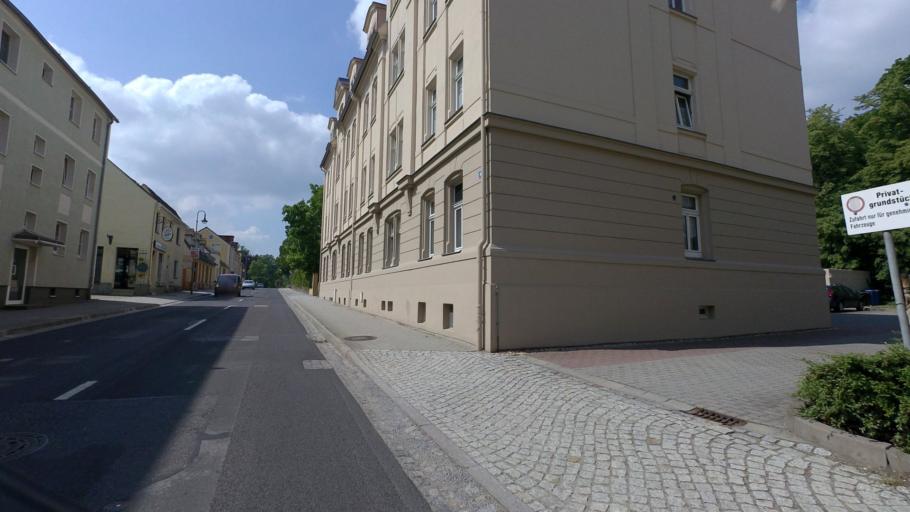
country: DE
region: Saxony
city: Niesky
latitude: 51.2927
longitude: 14.8206
